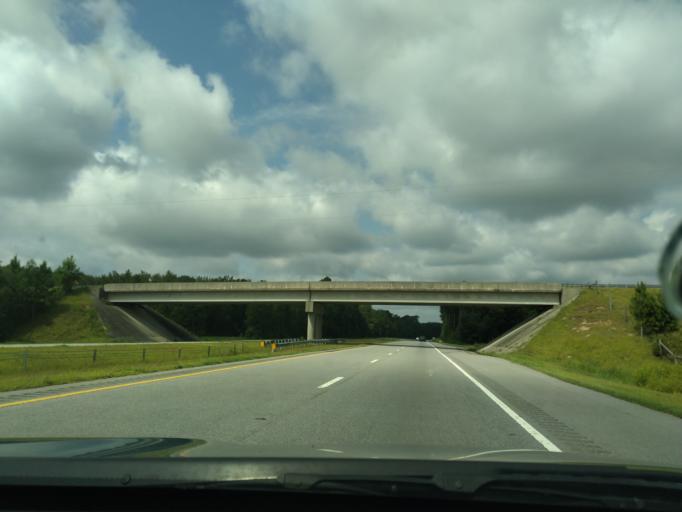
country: US
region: North Carolina
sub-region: Martin County
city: Robersonville
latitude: 35.8263
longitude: -77.1535
